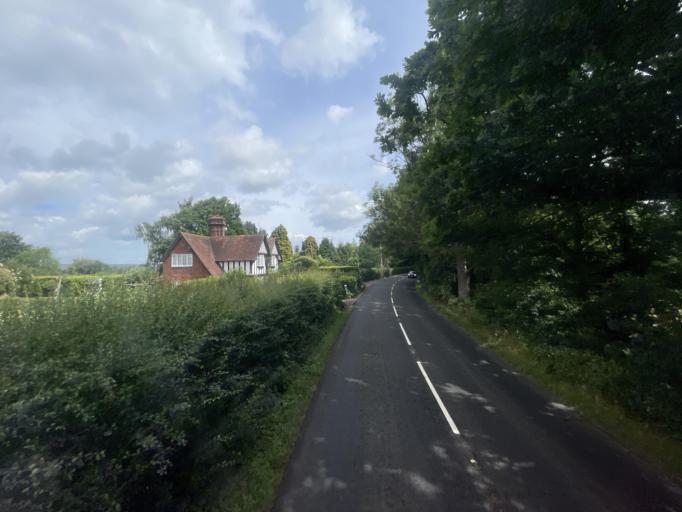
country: GB
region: England
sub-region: Kent
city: Sevenoaks
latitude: 51.1810
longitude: 0.1783
